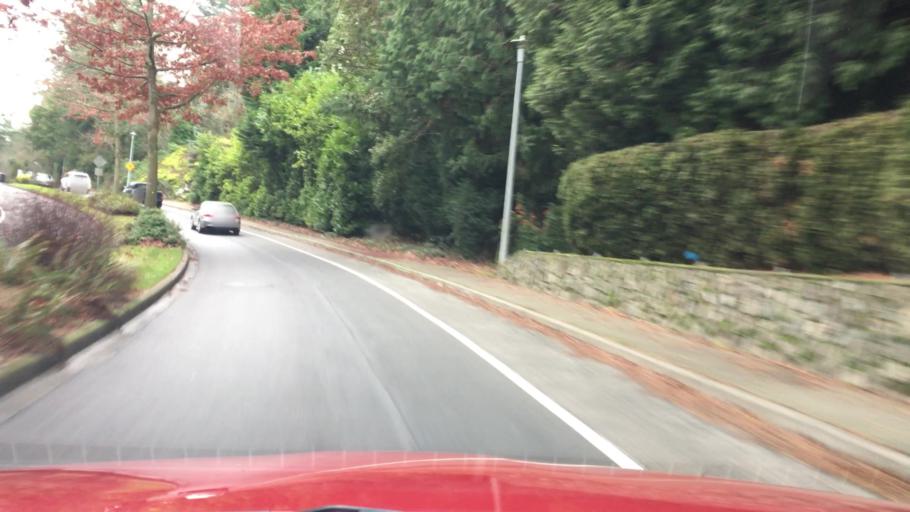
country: CA
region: British Columbia
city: Victoria
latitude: 48.5012
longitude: -123.3654
